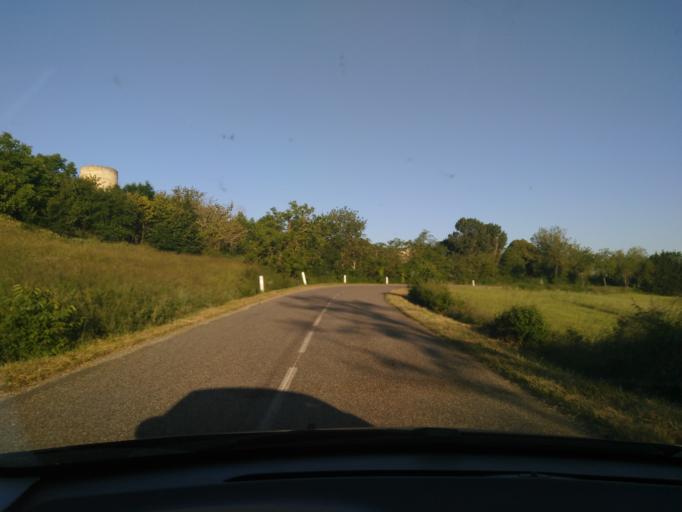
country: FR
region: Midi-Pyrenees
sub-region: Departement du Gers
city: Jegun
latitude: 43.8507
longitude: 0.5346
